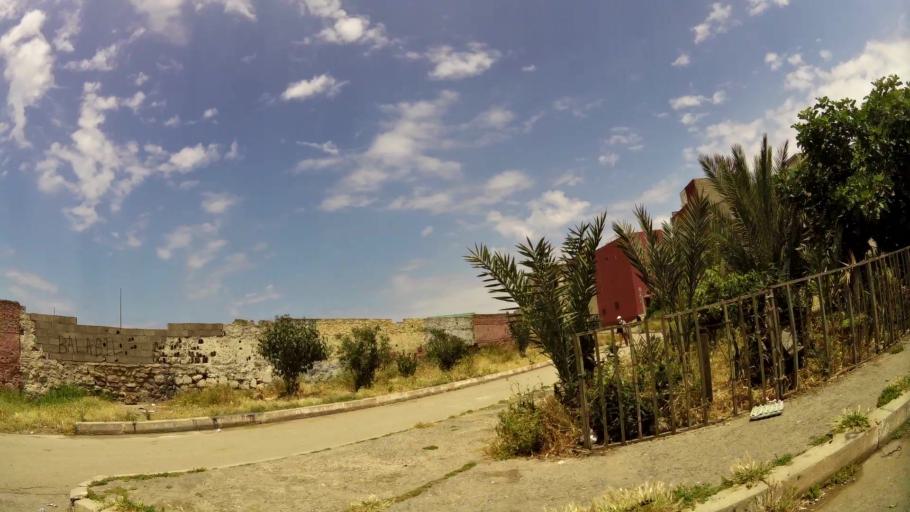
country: MA
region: Rabat-Sale-Zemmour-Zaer
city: Sale
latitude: 34.0473
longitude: -6.8227
